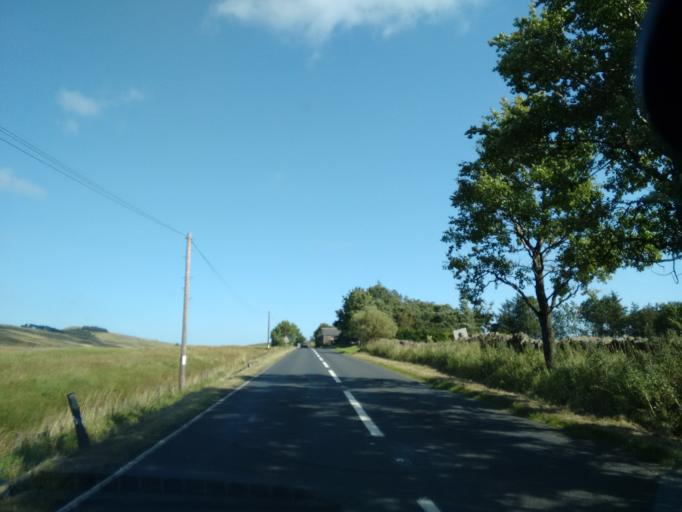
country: GB
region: England
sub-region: Northumberland
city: Bardon Mill
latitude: 54.9973
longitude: -2.3821
